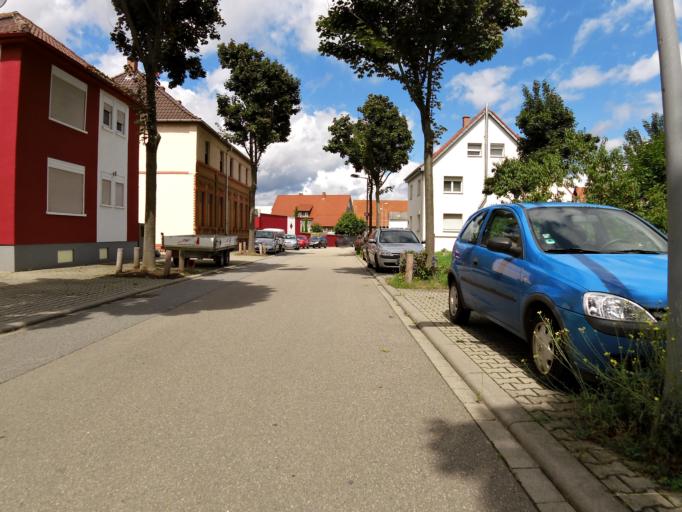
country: DE
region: Hesse
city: Lampertheim
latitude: 49.5588
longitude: 8.4469
